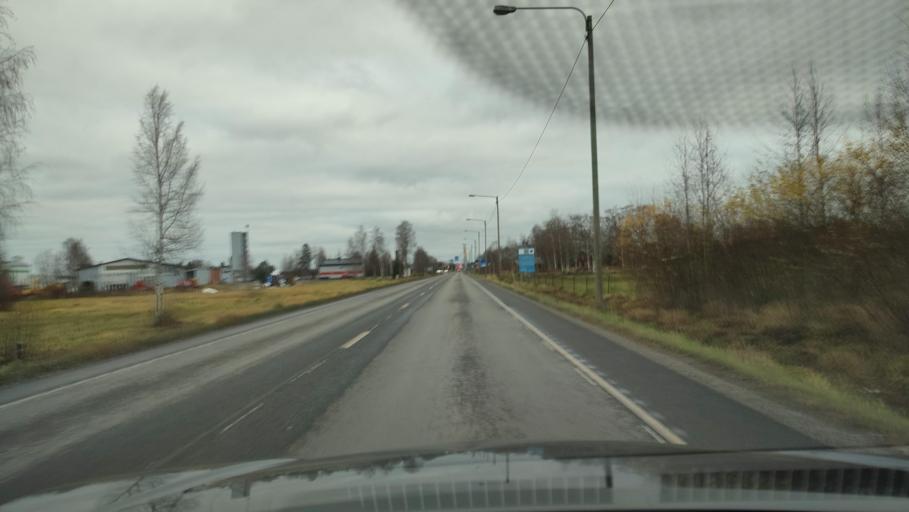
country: FI
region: Southern Ostrobothnia
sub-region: Seinaejoki
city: Ilmajoki
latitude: 62.7273
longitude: 22.5872
